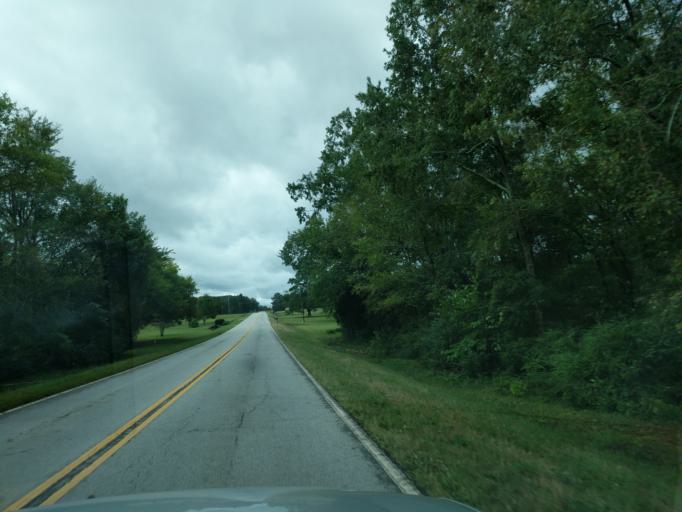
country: US
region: Georgia
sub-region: Elbert County
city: Elberton
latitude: 34.0323
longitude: -82.7944
